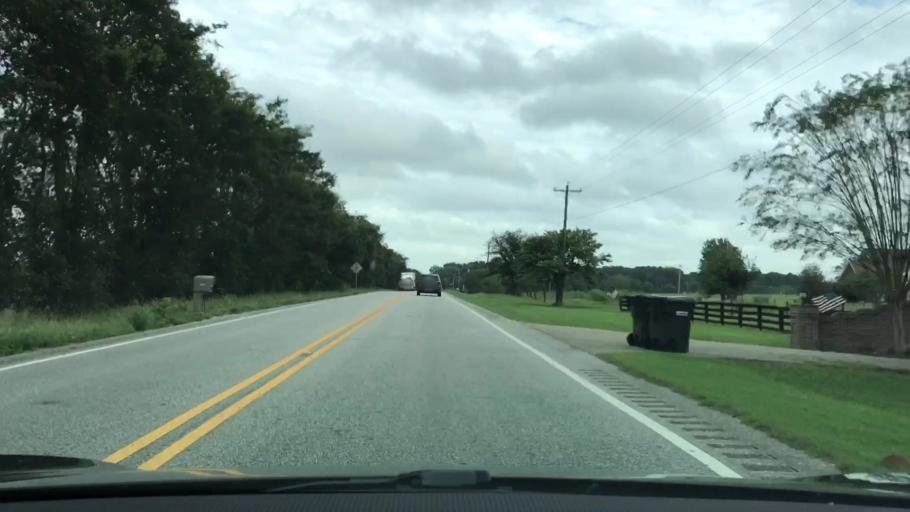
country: US
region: Alabama
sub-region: Montgomery County
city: Pike Road
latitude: 32.3192
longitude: -86.0480
